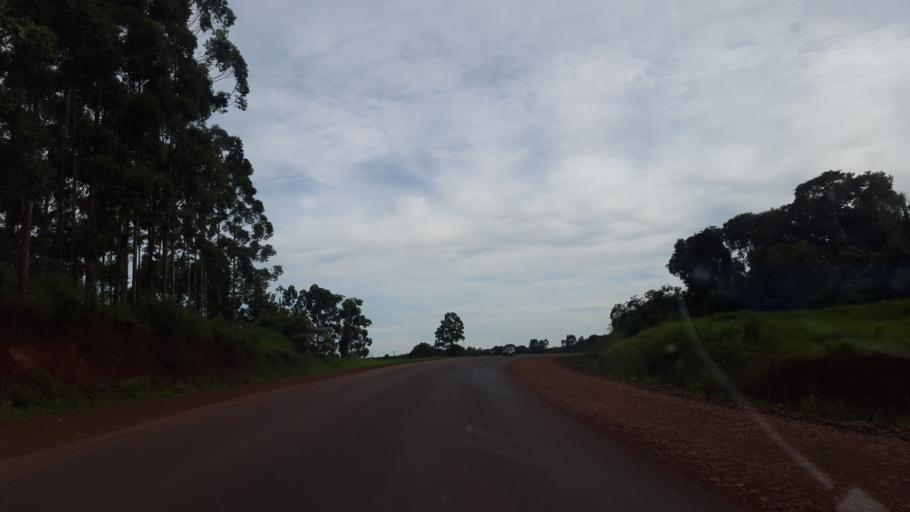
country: AR
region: Misiones
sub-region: Departamento de San Pedro
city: San Pedro
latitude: -26.4861
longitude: -53.8891
